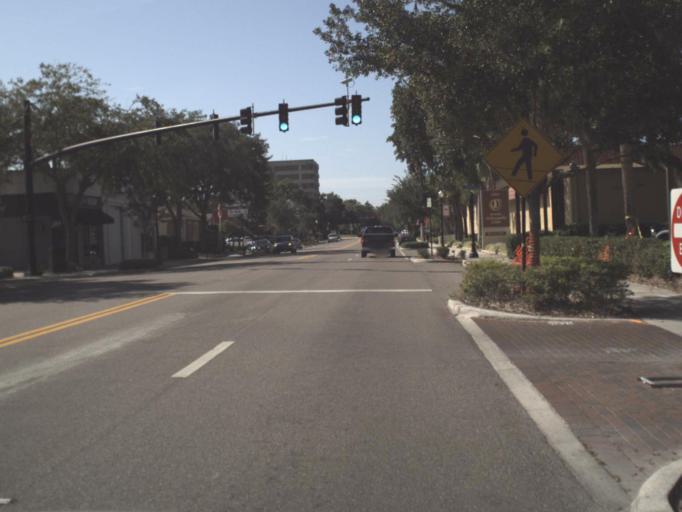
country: US
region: Florida
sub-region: Orange County
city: Winter Park
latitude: 28.5879
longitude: -81.3627
